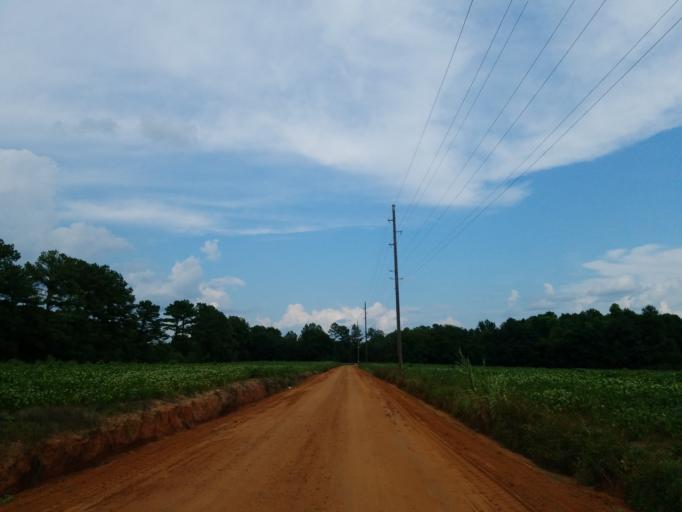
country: US
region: Georgia
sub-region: Dooly County
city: Unadilla
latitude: 32.2896
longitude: -83.7214
